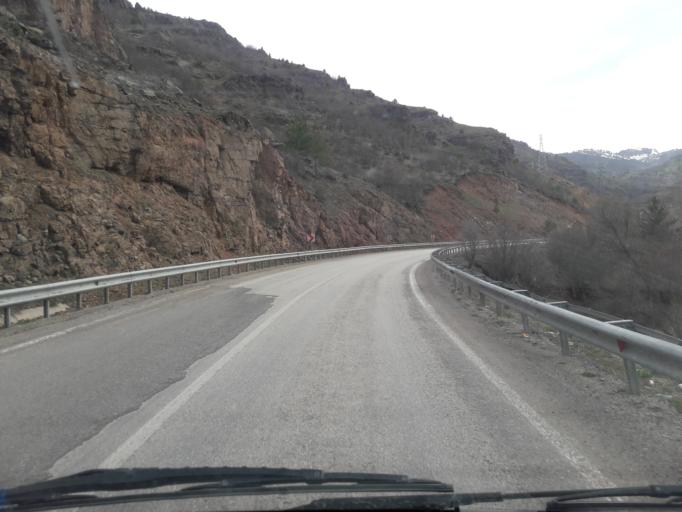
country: TR
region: Gumushane
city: Gumushkhane
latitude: 40.3053
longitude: 39.4770
